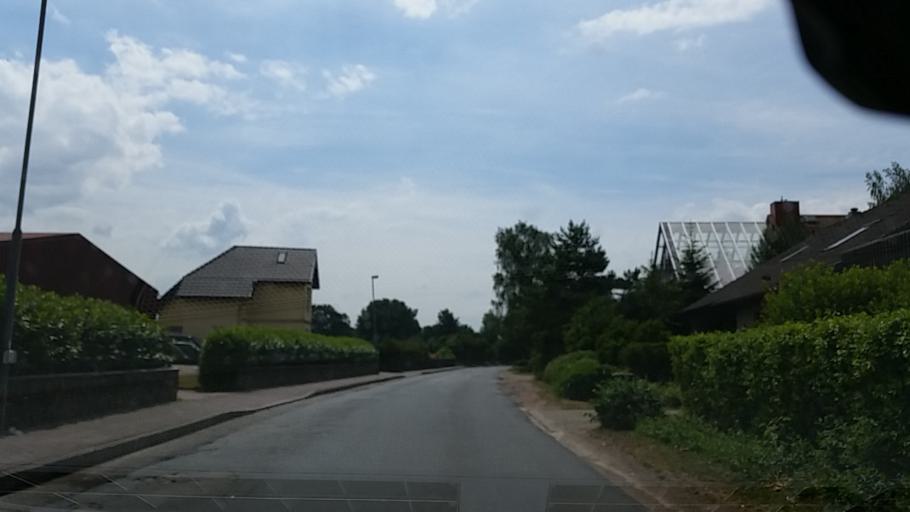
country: DE
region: Schleswig-Holstein
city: Tremsbuttel
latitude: 53.7416
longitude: 10.3091
